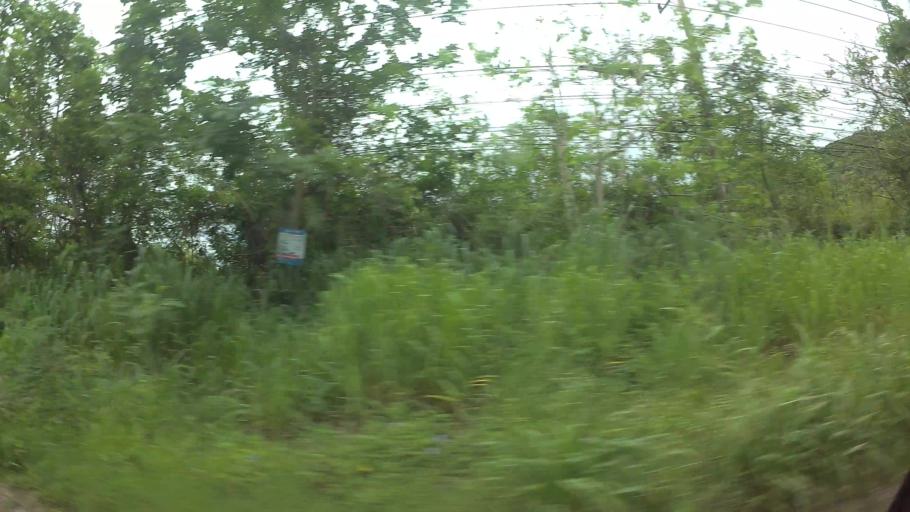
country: TH
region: Chon Buri
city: Si Racha
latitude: 13.2007
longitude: 100.9537
